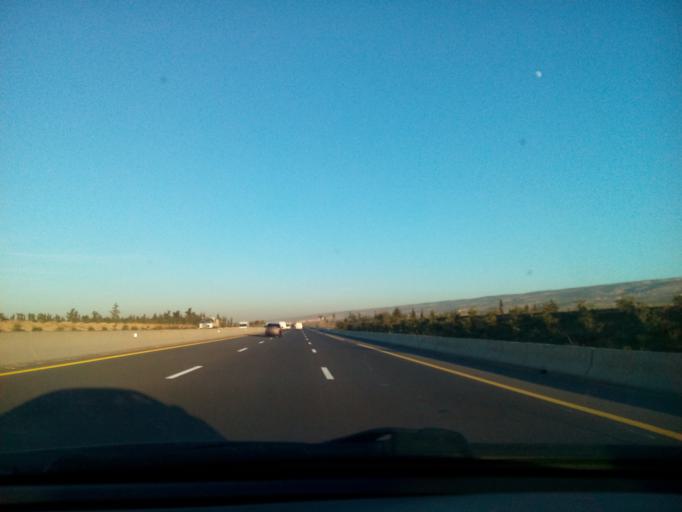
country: DZ
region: Relizane
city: Oued Rhiou
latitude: 35.9809
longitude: 0.9367
